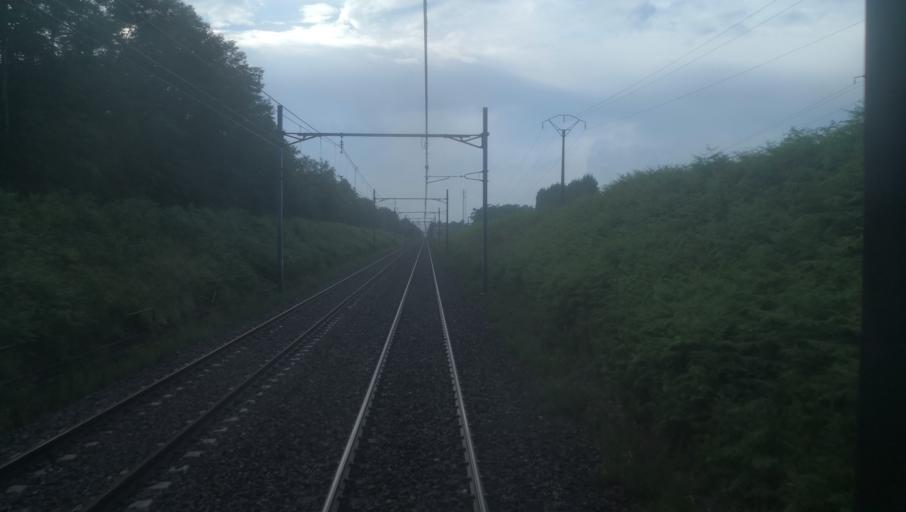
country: FR
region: Centre
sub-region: Departement du Loir-et-Cher
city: Lamotte-Beuvron
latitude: 47.6458
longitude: 1.9864
